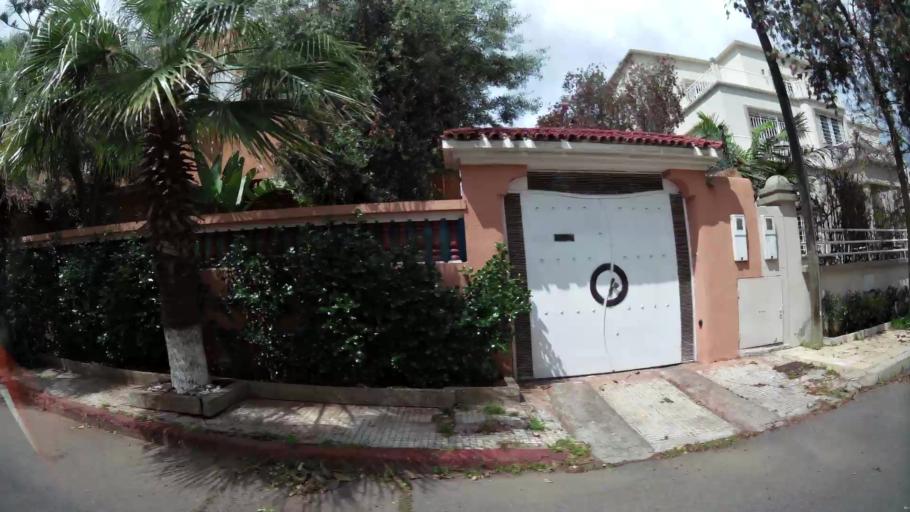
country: MA
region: Grand Casablanca
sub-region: Casablanca
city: Casablanca
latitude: 33.5606
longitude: -7.6226
